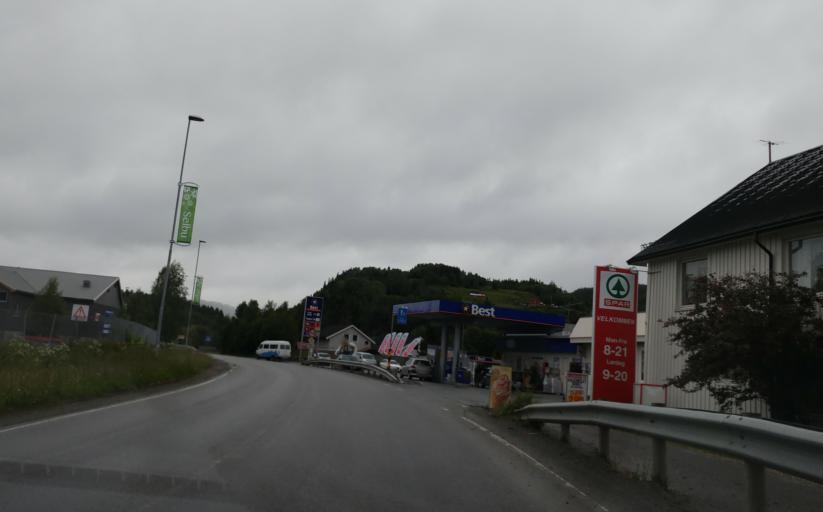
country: NO
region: Sor-Trondelag
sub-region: Selbu
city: Mebonden
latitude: 63.2502
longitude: 11.0946
